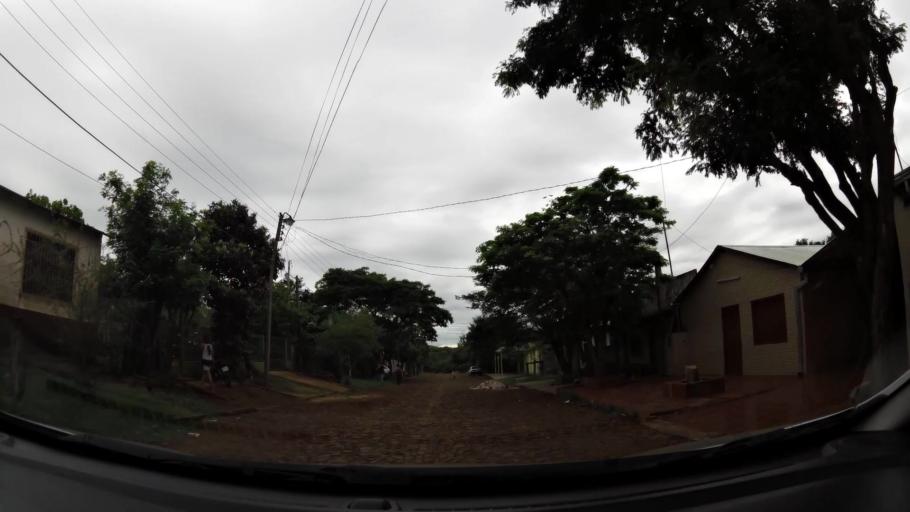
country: PY
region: Alto Parana
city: Ciudad del Este
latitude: -25.4390
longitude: -54.6419
